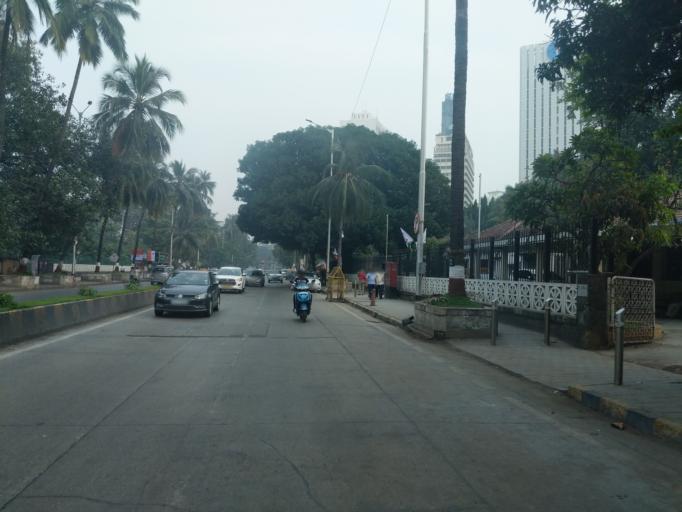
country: IN
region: Maharashtra
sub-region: Raigarh
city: Uran
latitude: 18.9281
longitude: 72.8243
